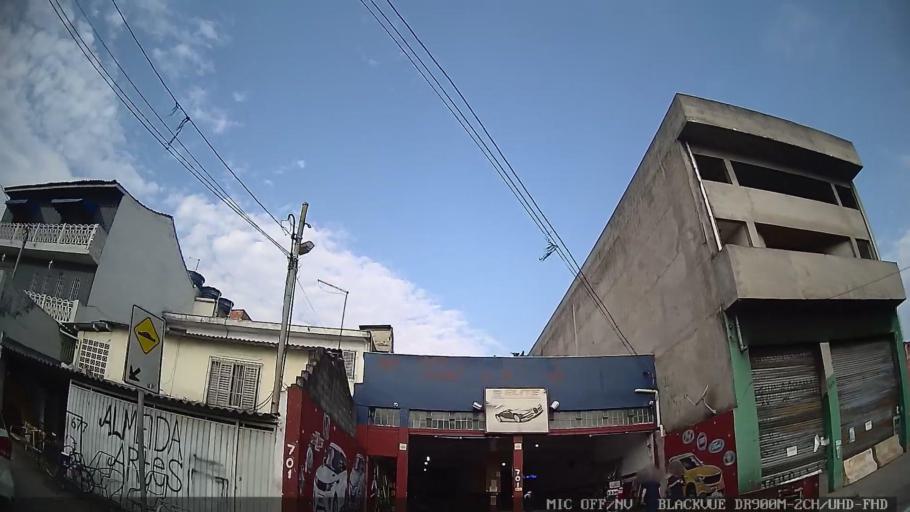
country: BR
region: Sao Paulo
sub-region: Ferraz De Vasconcelos
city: Ferraz de Vasconcelos
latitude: -23.5011
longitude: -46.4061
